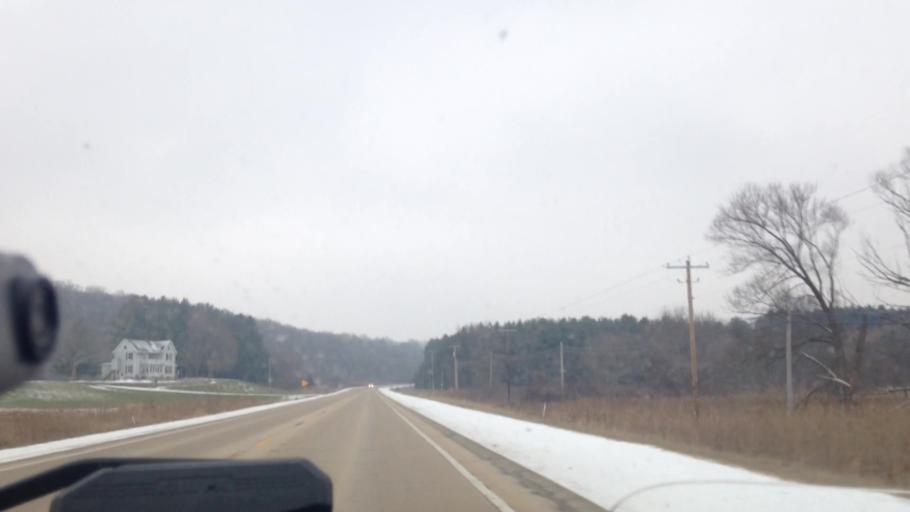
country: US
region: Wisconsin
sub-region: Dodge County
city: Mayville
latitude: 43.4592
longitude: -88.5442
